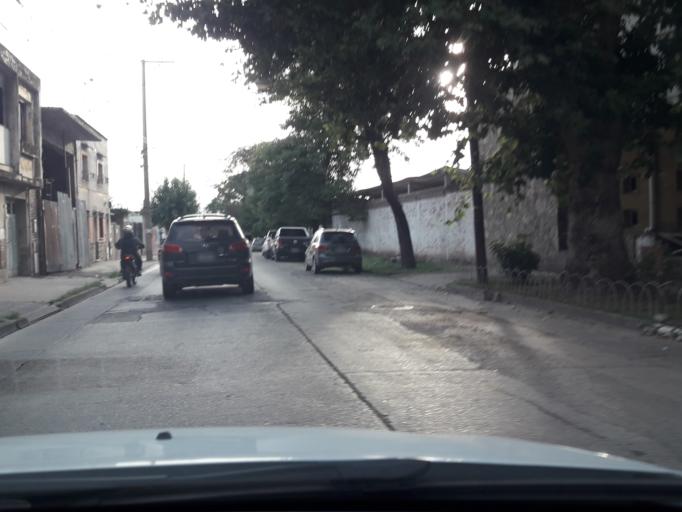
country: AR
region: Jujuy
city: San Salvador de Jujuy
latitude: -24.1907
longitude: -65.3095
